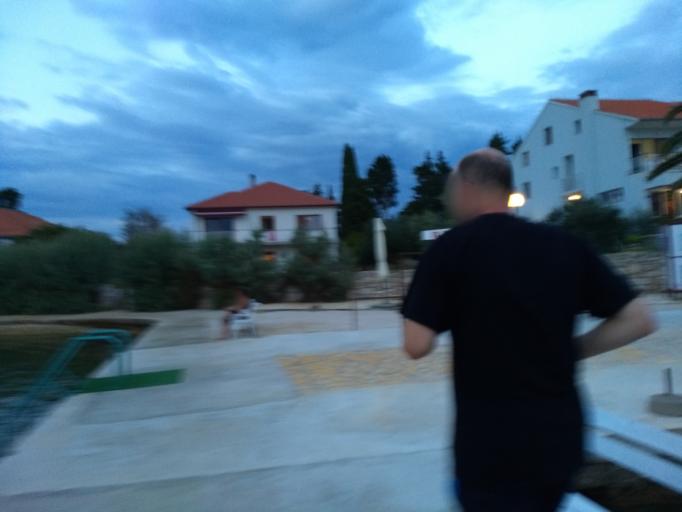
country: HR
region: Zadarska
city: Ugljan
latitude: 44.1380
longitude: 15.0722
